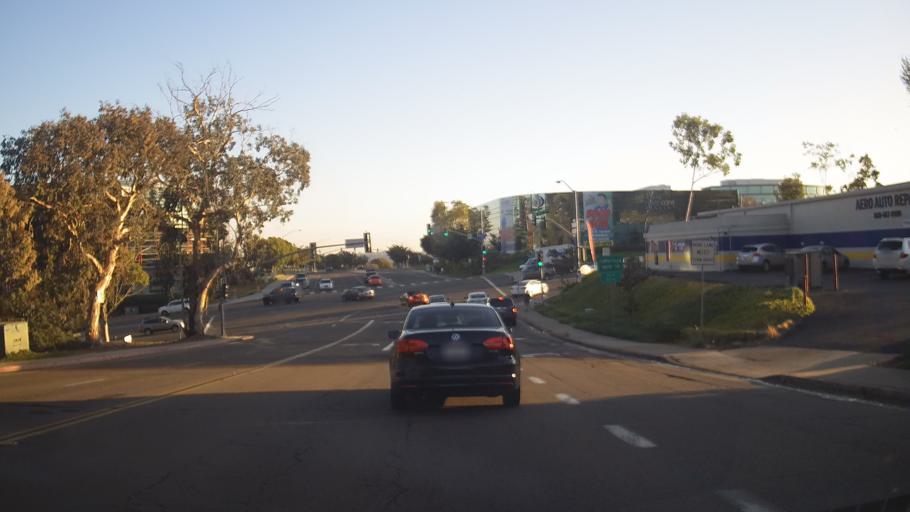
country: US
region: California
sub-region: San Diego County
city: San Diego
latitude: 32.8095
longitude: -117.1193
